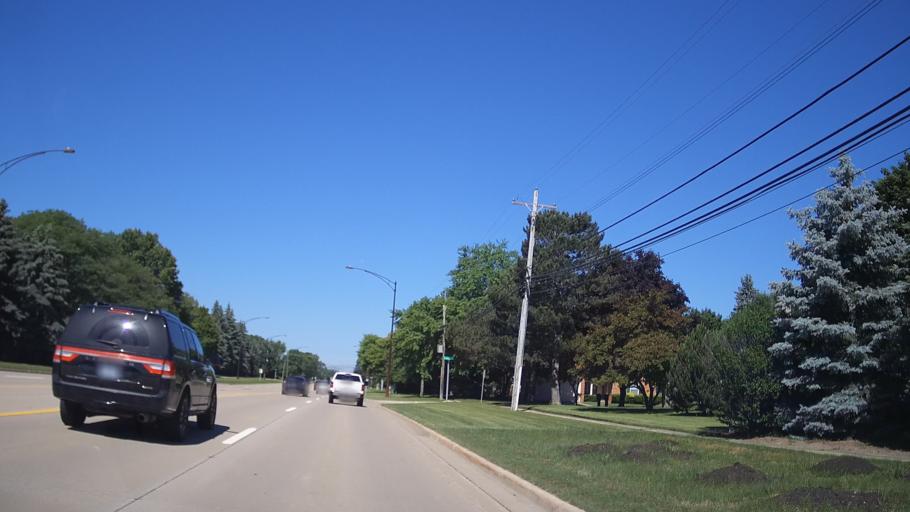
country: US
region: Michigan
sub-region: Oakland County
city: Troy
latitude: 42.5924
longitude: -83.1176
